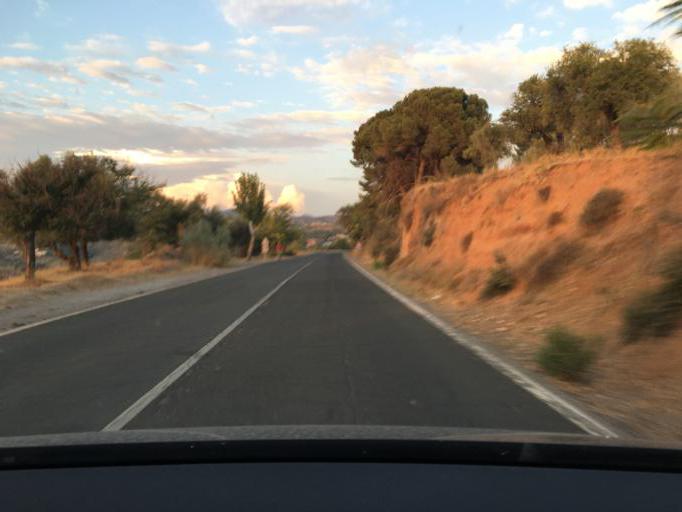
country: ES
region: Andalusia
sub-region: Provincia de Granada
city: Jun
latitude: 37.1980
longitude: -3.5805
